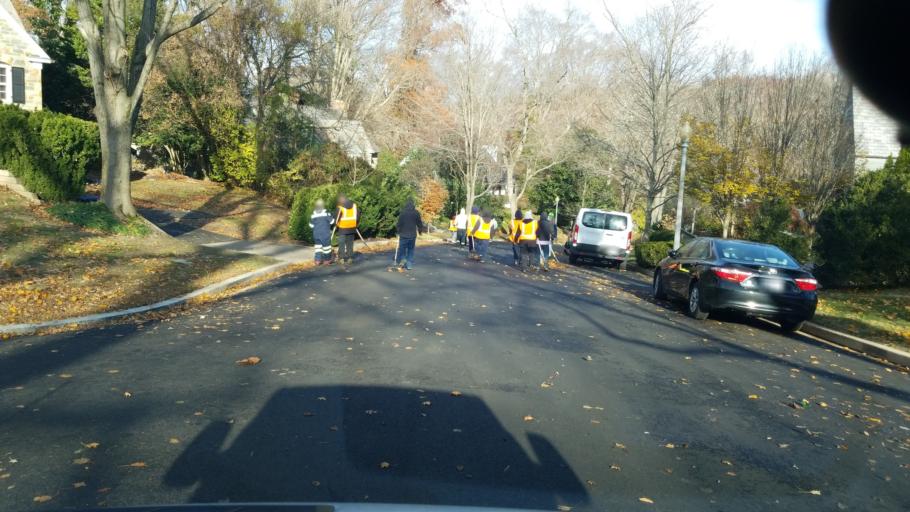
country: US
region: Maryland
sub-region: Montgomery County
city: Brookmont
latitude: 38.9371
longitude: -77.1032
